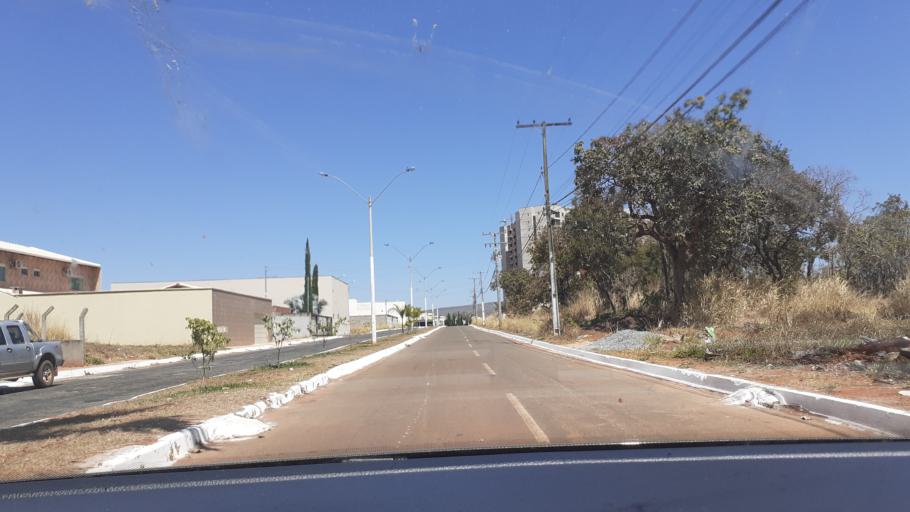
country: BR
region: Goias
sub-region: Caldas Novas
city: Caldas Novas
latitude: -17.7390
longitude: -48.6356
